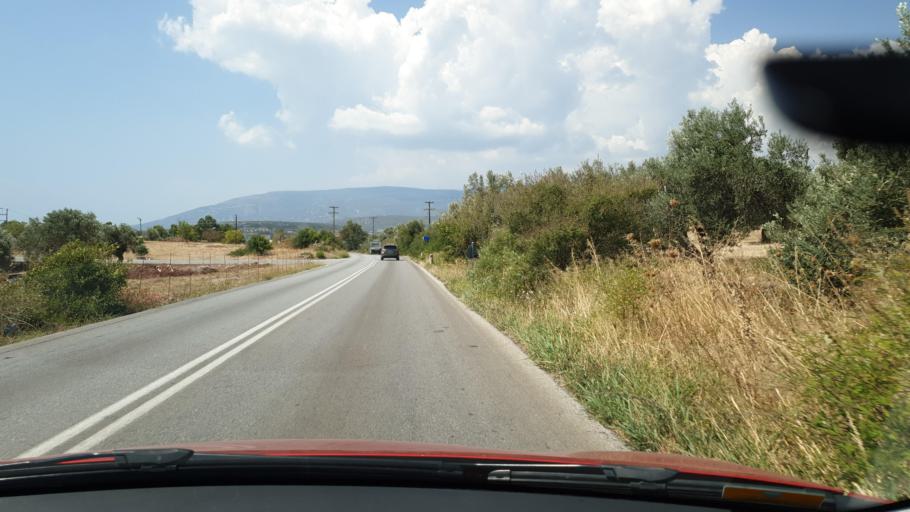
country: GR
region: Central Greece
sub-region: Nomos Evvoias
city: Aliveri
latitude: 38.3942
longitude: 24.0738
